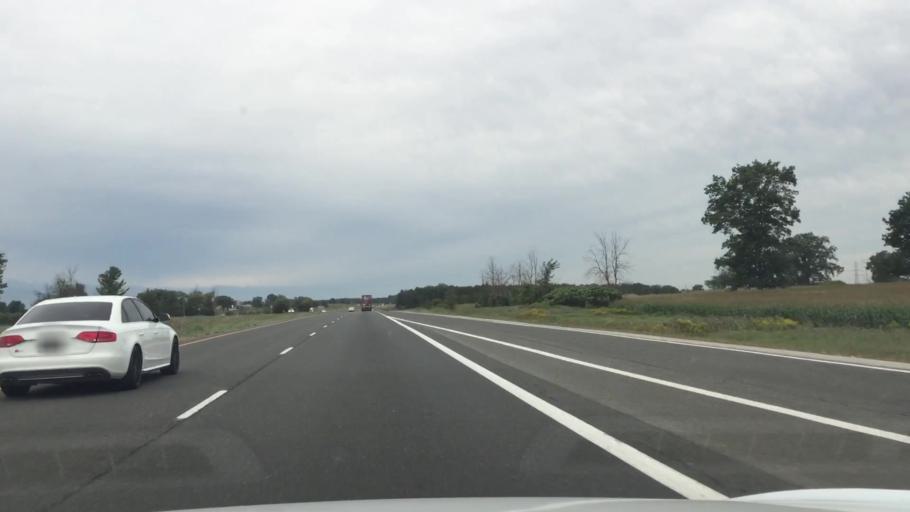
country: CA
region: Ontario
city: London
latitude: 42.8916
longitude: -81.2983
